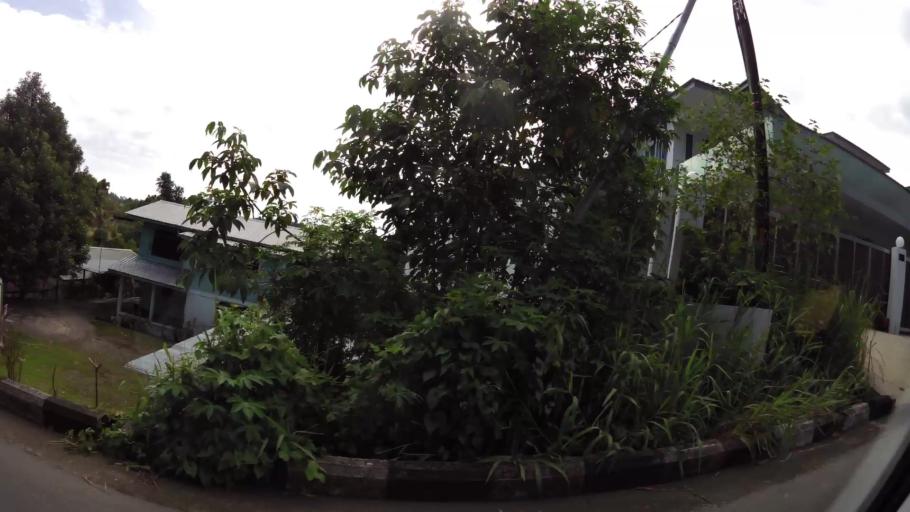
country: BN
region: Brunei and Muara
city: Bandar Seri Begawan
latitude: 4.8991
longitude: 114.8958
